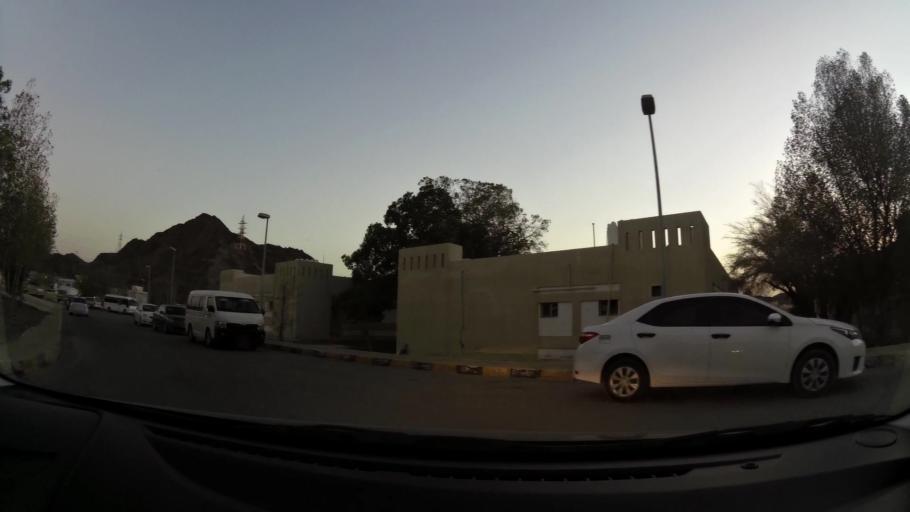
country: OM
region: Muhafazat Masqat
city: Muscat
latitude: 23.5927
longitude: 58.5678
